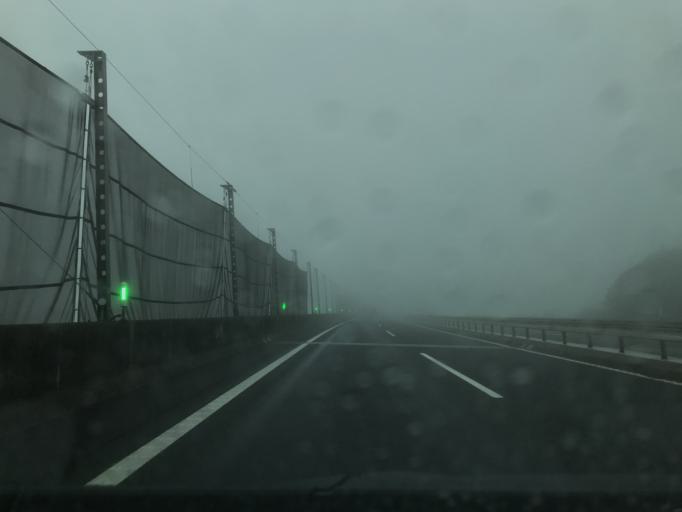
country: JP
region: Oita
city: Beppu
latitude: 33.3268
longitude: 131.4611
